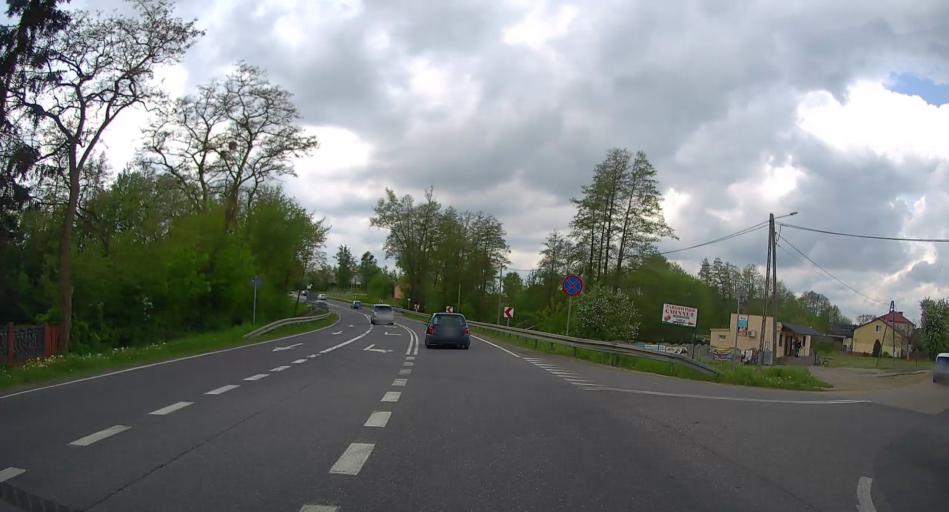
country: PL
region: Masovian Voivodeship
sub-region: Powiat plonski
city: Zaluski
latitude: 52.4315
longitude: 20.4543
